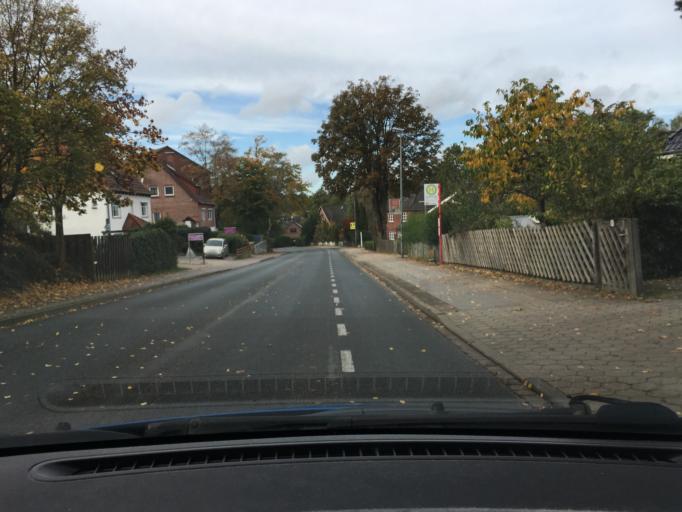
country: DE
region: Lower Saxony
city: Buchholz in der Nordheide
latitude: 53.3253
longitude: 9.8660
